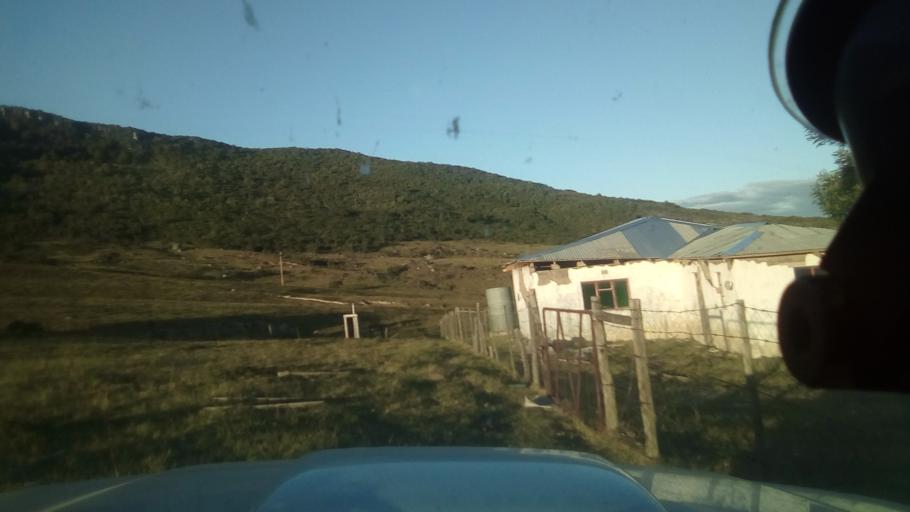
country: ZA
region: Eastern Cape
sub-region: Buffalo City Metropolitan Municipality
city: Bhisho
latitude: -32.7348
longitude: 27.3790
